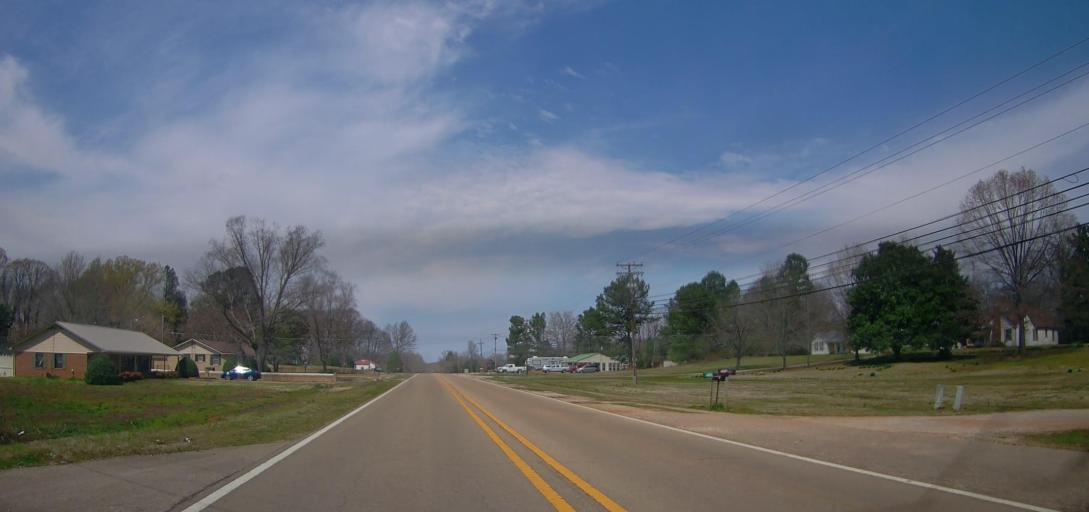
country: US
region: Mississippi
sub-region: Union County
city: New Albany
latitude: 34.4551
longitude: -88.9745
